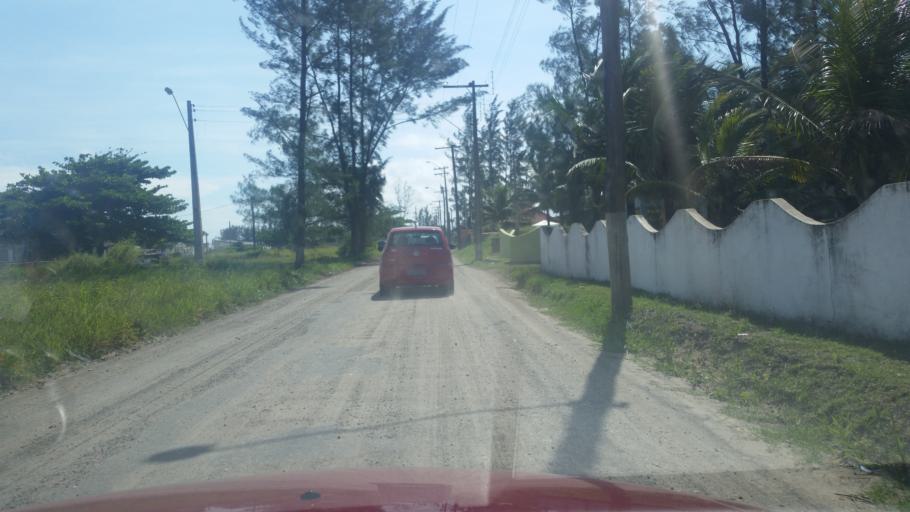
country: BR
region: Sao Paulo
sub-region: Iguape
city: Iguape
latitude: -24.6966
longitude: -47.4525
